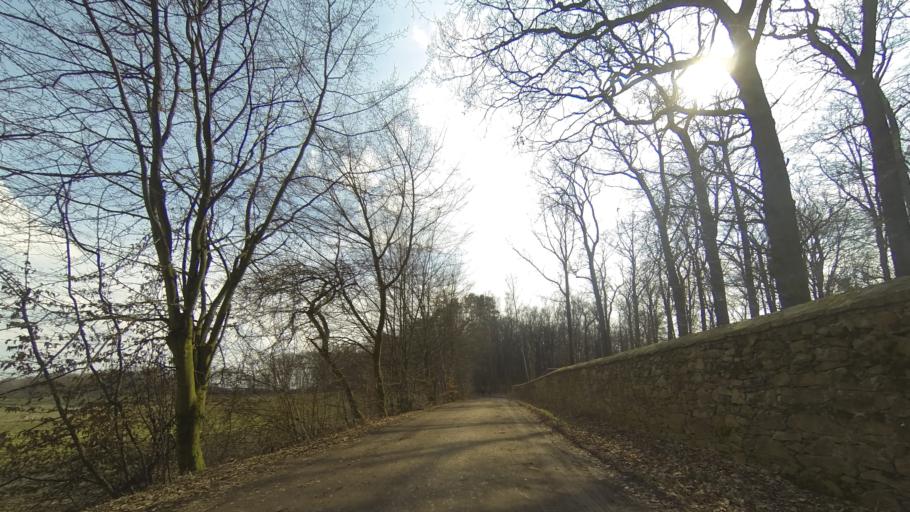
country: DE
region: Saxony
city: Moritzburg
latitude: 51.1741
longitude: 13.7033
